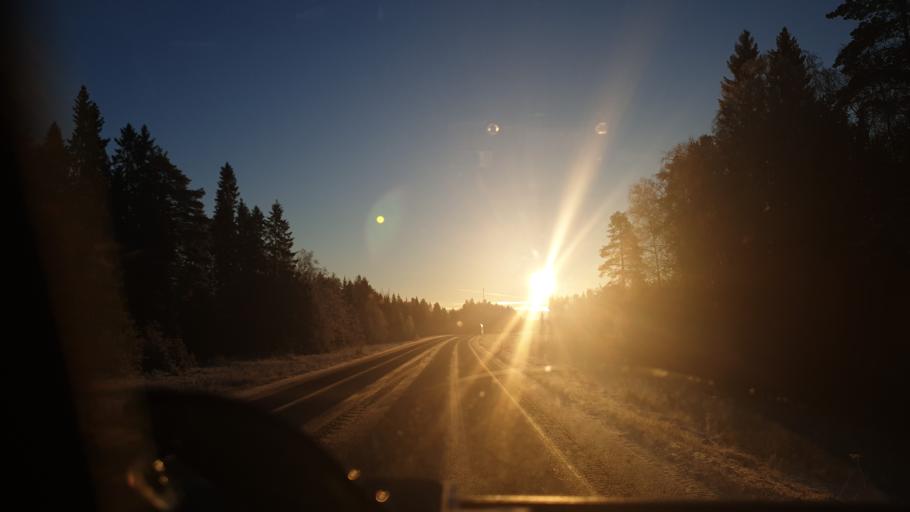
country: FI
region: Northern Ostrobothnia
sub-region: Ylivieska
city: Kalajoki
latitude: 64.2922
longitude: 23.9430
